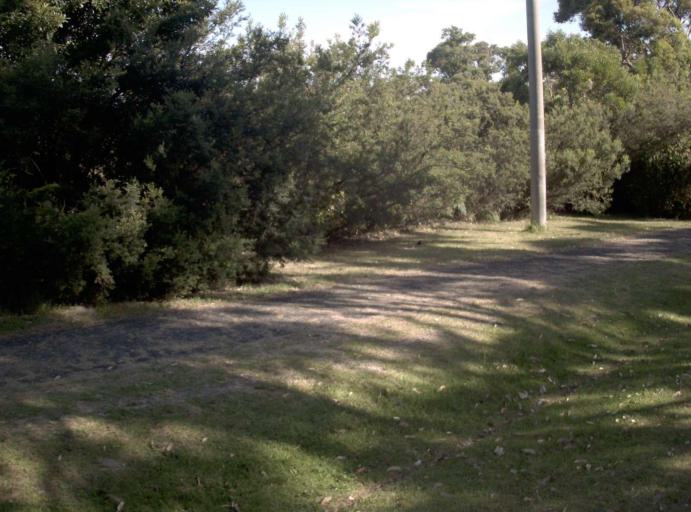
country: AU
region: Victoria
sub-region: East Gippsland
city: Lakes Entrance
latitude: -37.7930
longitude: 148.5343
